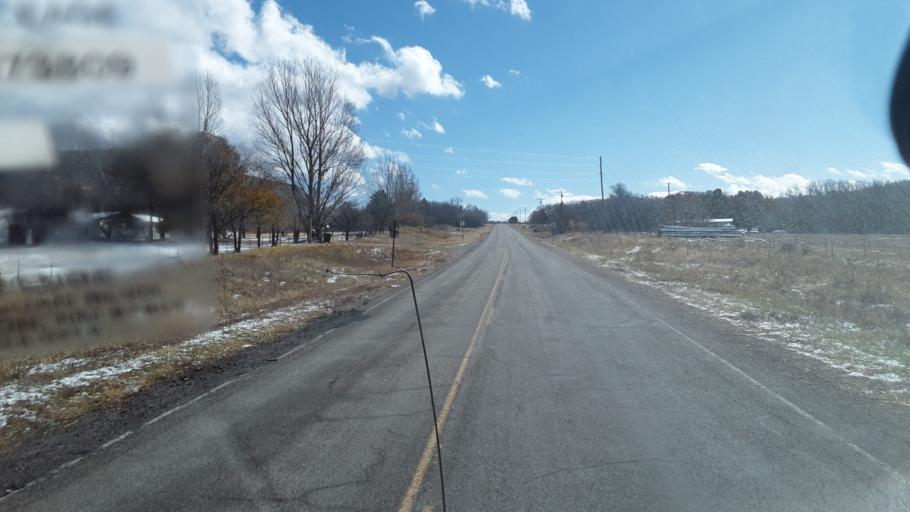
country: US
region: New Mexico
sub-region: Rio Arriba County
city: Santa Teresa
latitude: 36.2272
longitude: -106.7999
